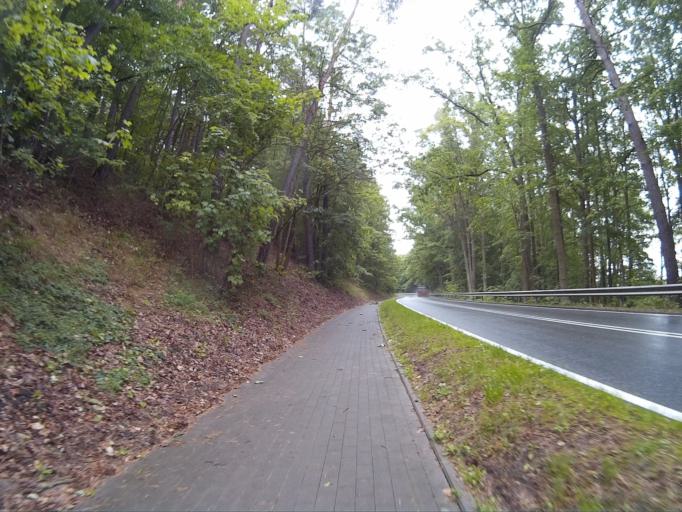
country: PL
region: Kujawsko-Pomorskie
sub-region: Powiat swiecki
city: Osie
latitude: 53.6160
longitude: 18.2753
